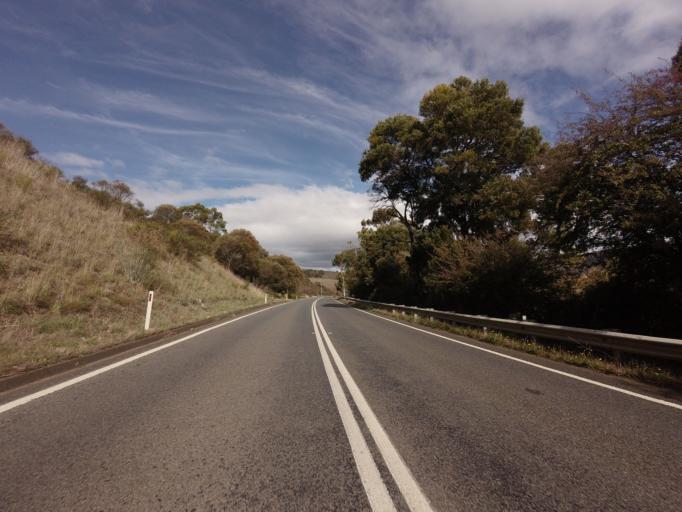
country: AU
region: Tasmania
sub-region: Derwent Valley
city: New Norfolk
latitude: -42.7274
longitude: 146.9556
